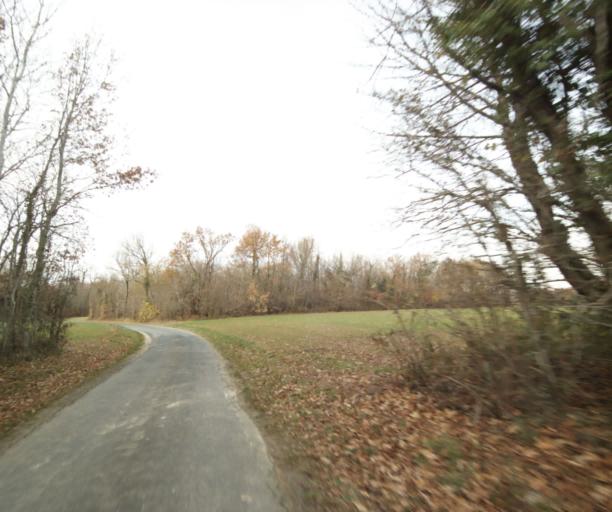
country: FR
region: Poitou-Charentes
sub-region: Departement de la Charente-Maritime
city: Fontcouverte
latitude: 45.7940
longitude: -0.6023
